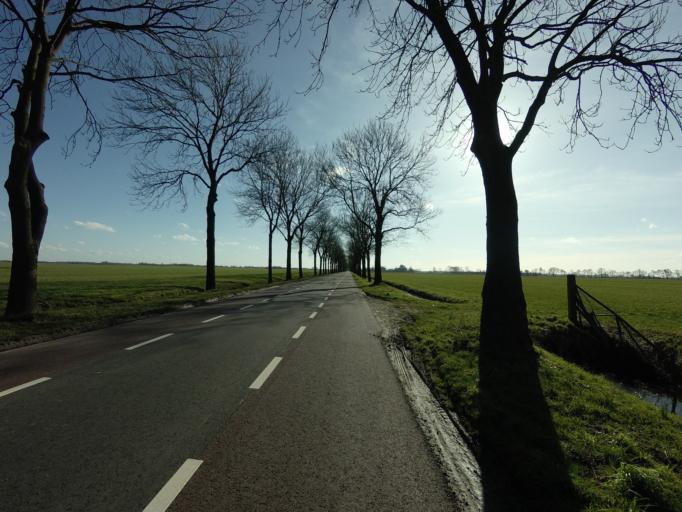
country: NL
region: Utrecht
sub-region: Gemeente Montfoort
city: Montfoort
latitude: 52.0750
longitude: 4.9593
